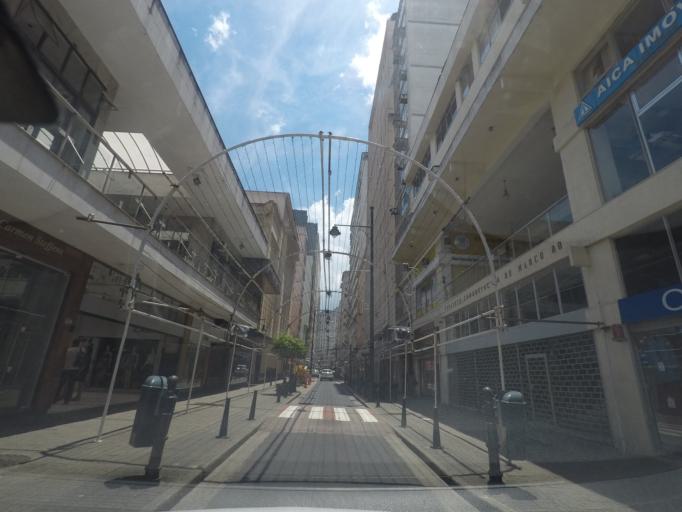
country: BR
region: Rio de Janeiro
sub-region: Petropolis
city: Petropolis
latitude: -22.5098
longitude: -43.1769
